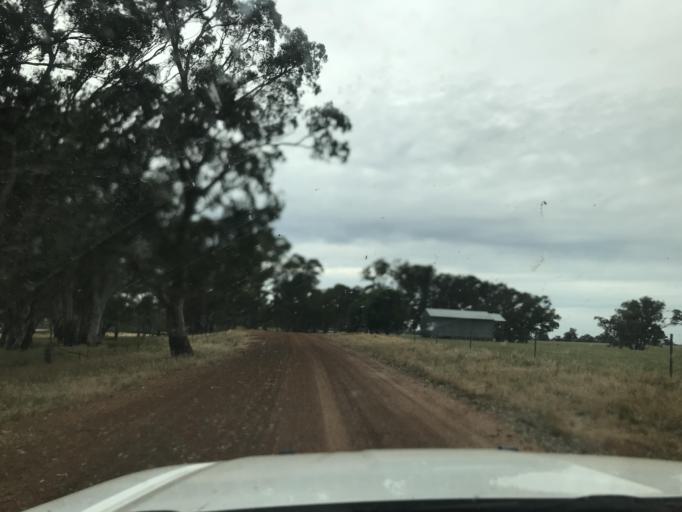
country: AU
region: Victoria
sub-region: Horsham
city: Horsham
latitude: -37.0786
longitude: 141.6662
